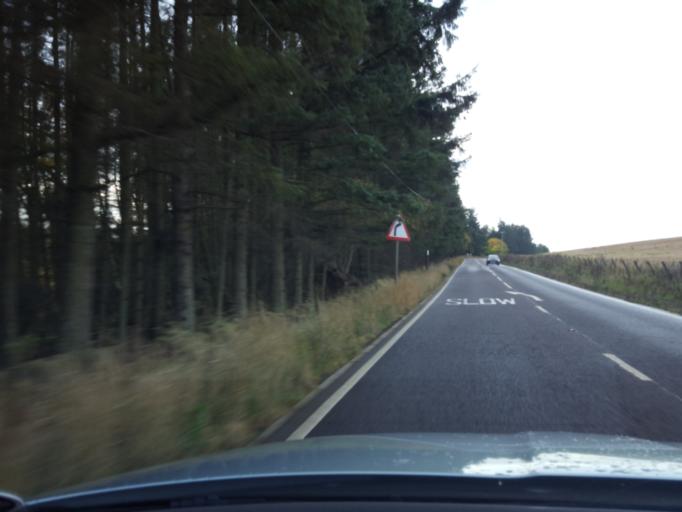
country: GB
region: Scotland
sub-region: South Lanarkshire
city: Carnwath
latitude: 55.7199
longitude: -3.5843
